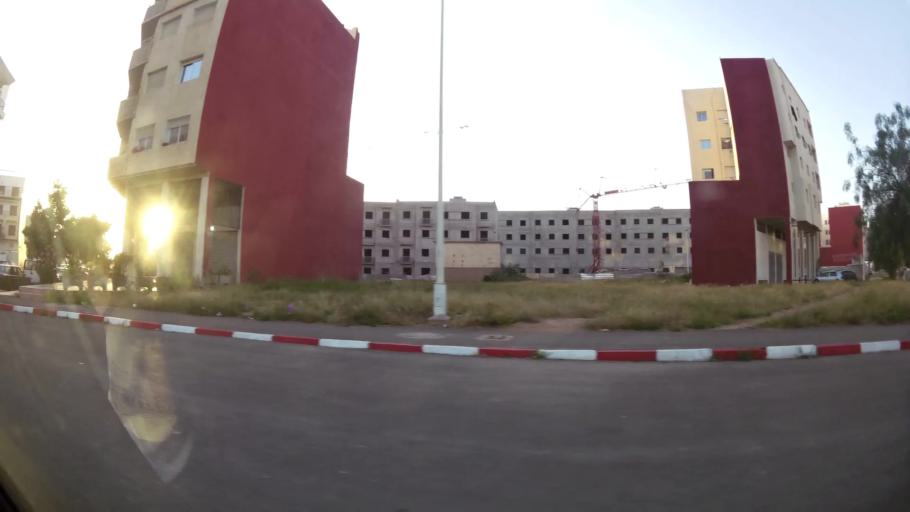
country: MA
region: Oued ed Dahab-Lagouira
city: Dakhla
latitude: 30.3932
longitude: -9.5658
